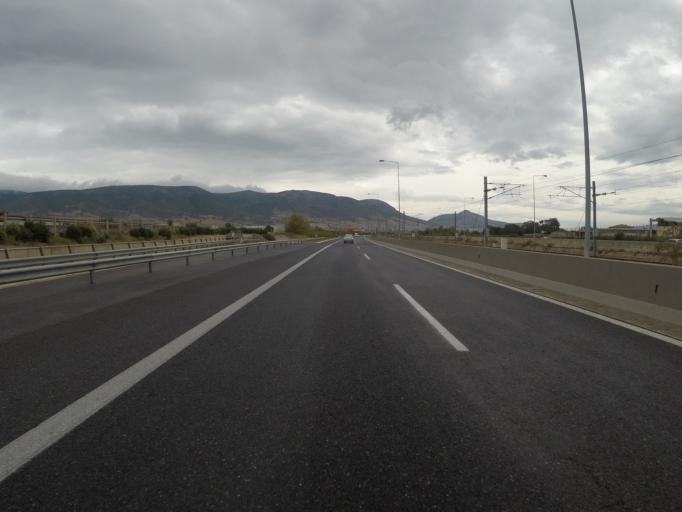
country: GR
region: Attica
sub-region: Nomarchia Dytikis Attikis
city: Magoula
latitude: 38.0919
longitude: 23.5554
